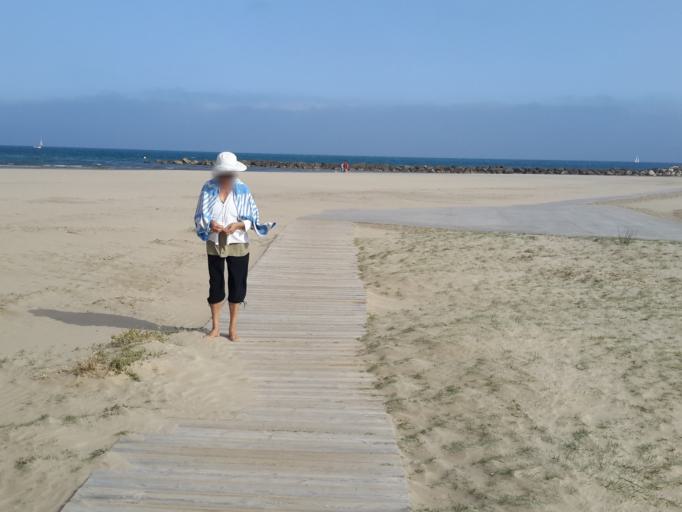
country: ES
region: Catalonia
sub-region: Provincia de Barcelona
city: Vilanova i la Geltru
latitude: 41.2114
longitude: 1.7184
